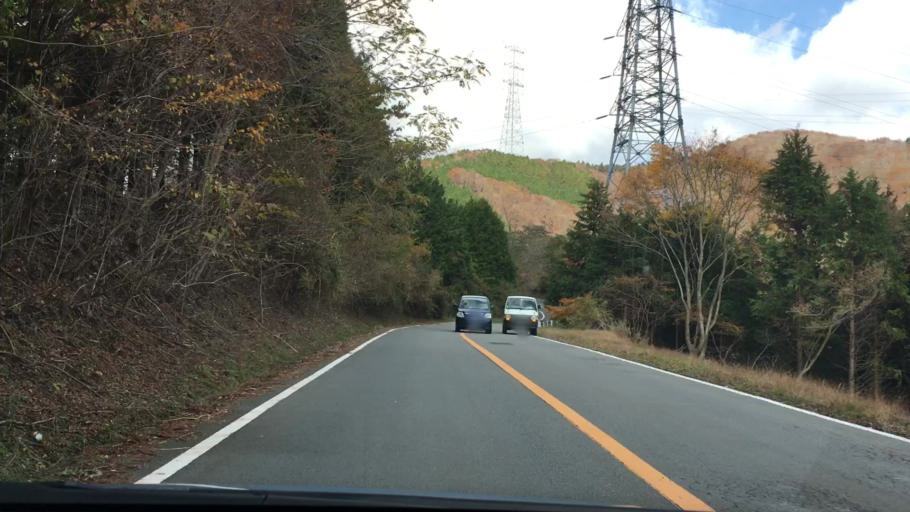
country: JP
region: Shizuoka
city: Gotemba
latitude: 35.3931
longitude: 138.9430
